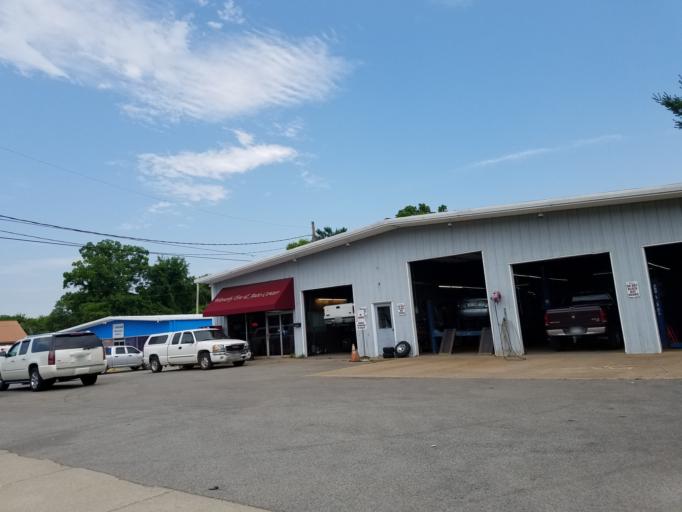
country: US
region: Tennessee
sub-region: Humphreys County
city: Waverly
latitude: 36.0839
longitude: -87.8014
